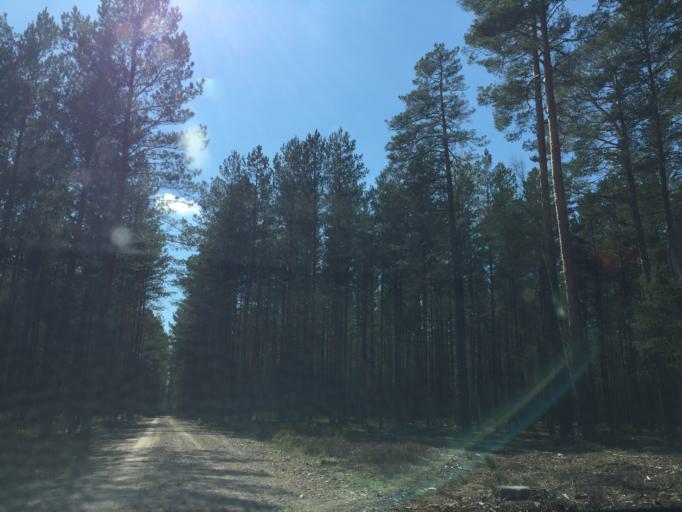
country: LV
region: Strenci
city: Strenci
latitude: 57.5937
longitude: 25.6990
